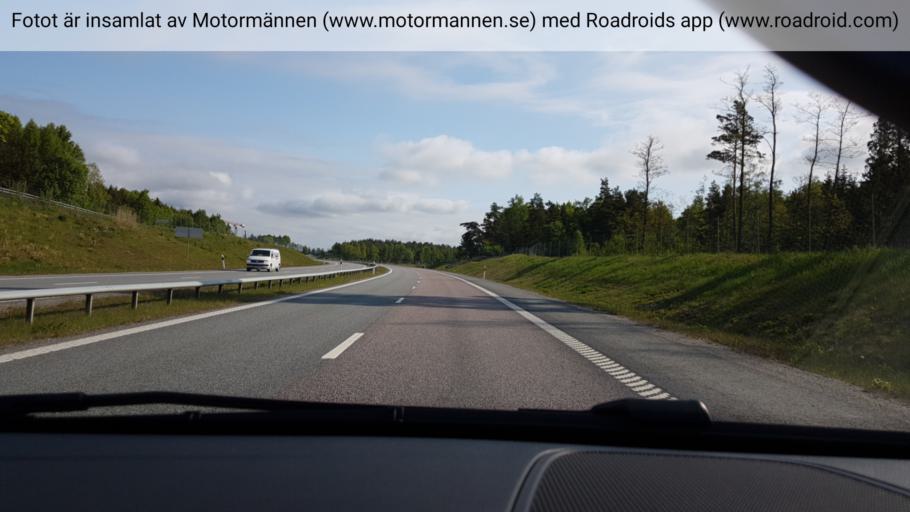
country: SE
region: Stockholm
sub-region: Haninge Kommun
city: Jordbro
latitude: 59.0777
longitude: 18.0758
